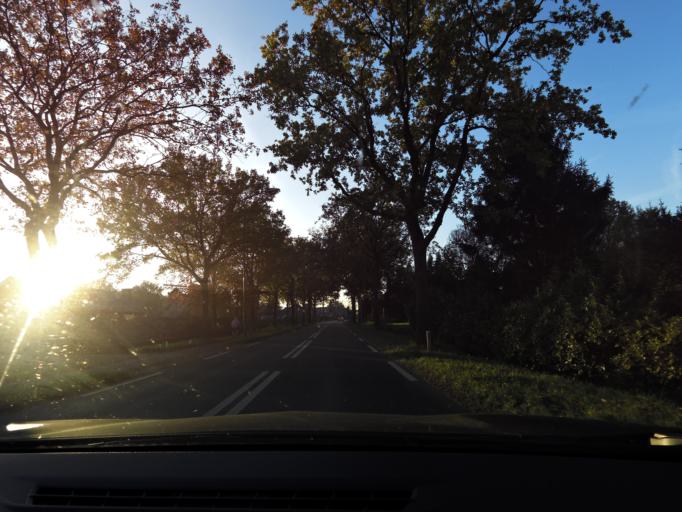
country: NL
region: North Brabant
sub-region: Gemeente Rucphen
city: Rucphen
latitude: 51.5770
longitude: 4.5937
